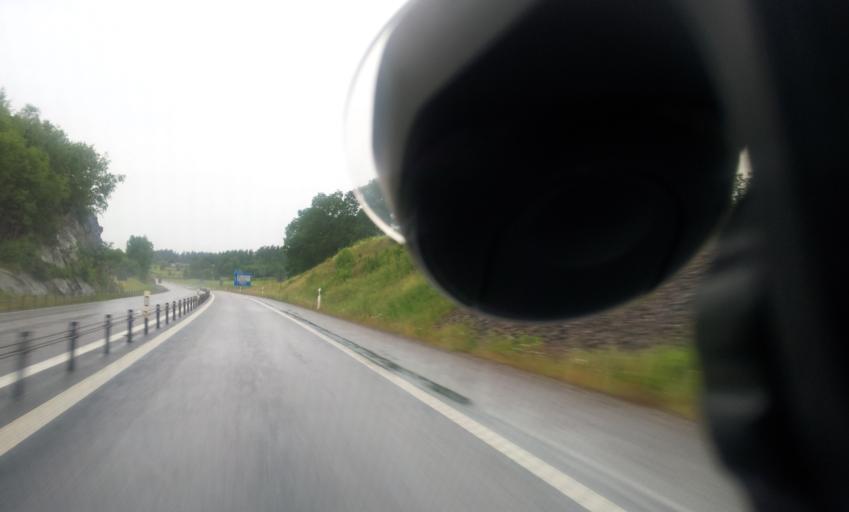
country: SE
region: OEstergoetland
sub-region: Valdemarsviks Kommun
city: Gusum
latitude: 58.2752
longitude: 16.5155
